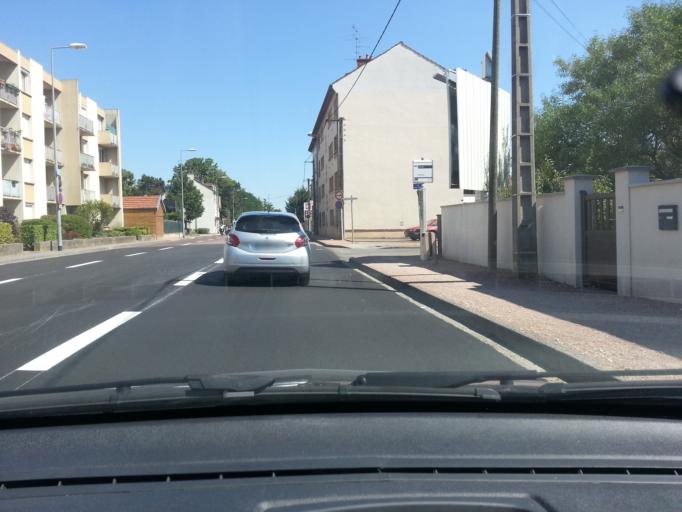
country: FR
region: Bourgogne
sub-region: Departement de la Cote-d'Or
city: Dijon
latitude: 47.3079
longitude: 5.0414
